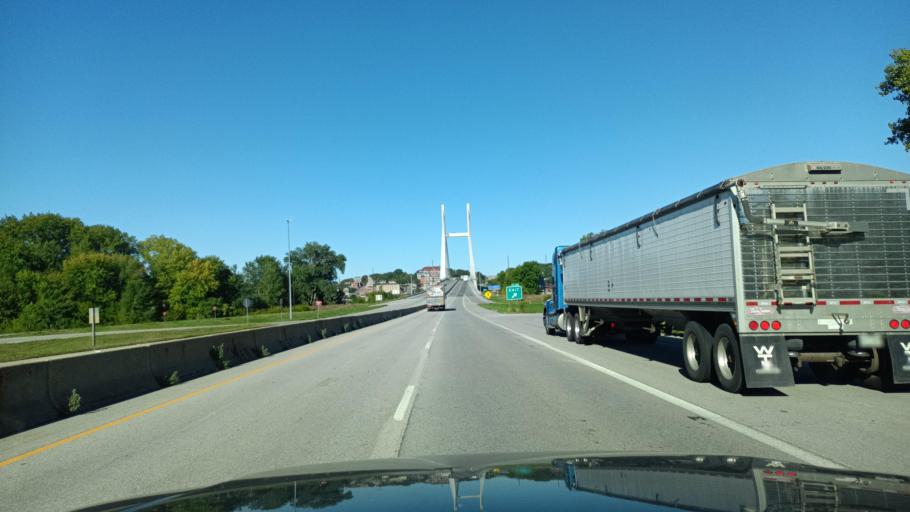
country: US
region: Iowa
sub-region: Des Moines County
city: Burlington
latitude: 40.8102
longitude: -91.0879
